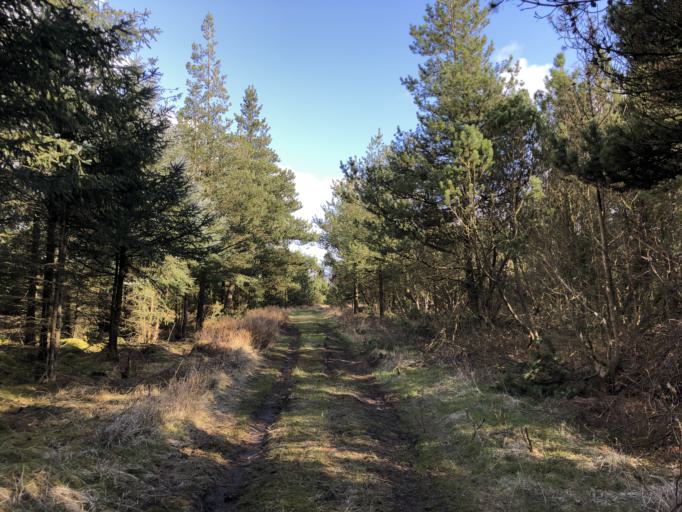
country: DK
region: Central Jutland
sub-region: Holstebro Kommune
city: Ulfborg
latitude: 56.2745
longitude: 8.3503
